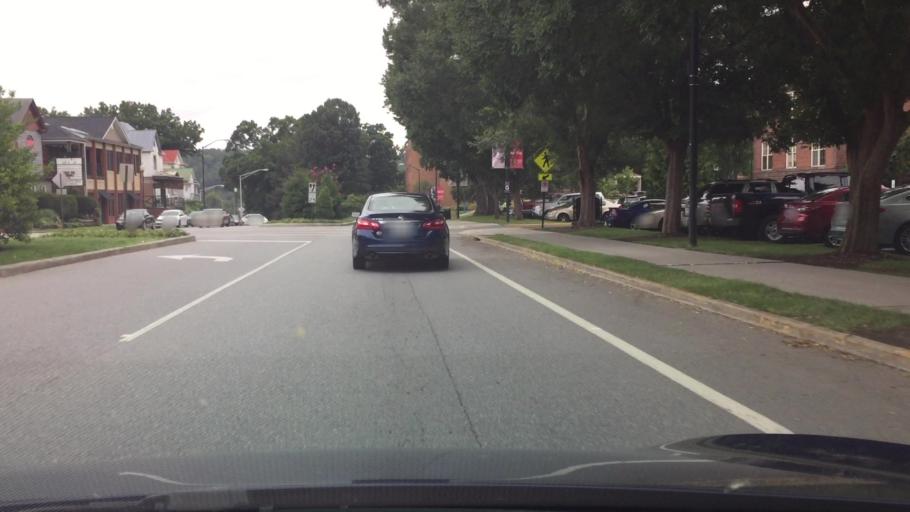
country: US
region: Virginia
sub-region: City of Radford
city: Radford
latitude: 37.1385
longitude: -80.5531
